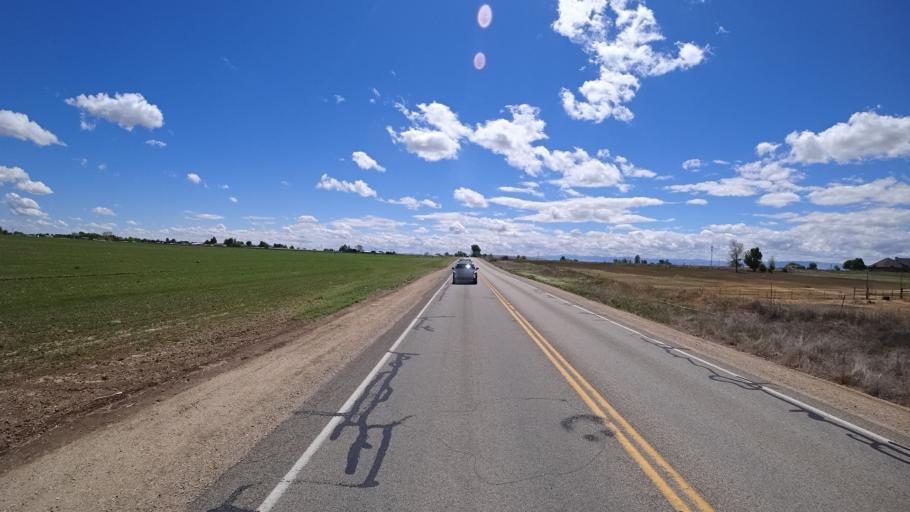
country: US
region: Idaho
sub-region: Ada County
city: Meridian
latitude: 43.5665
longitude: -116.4338
